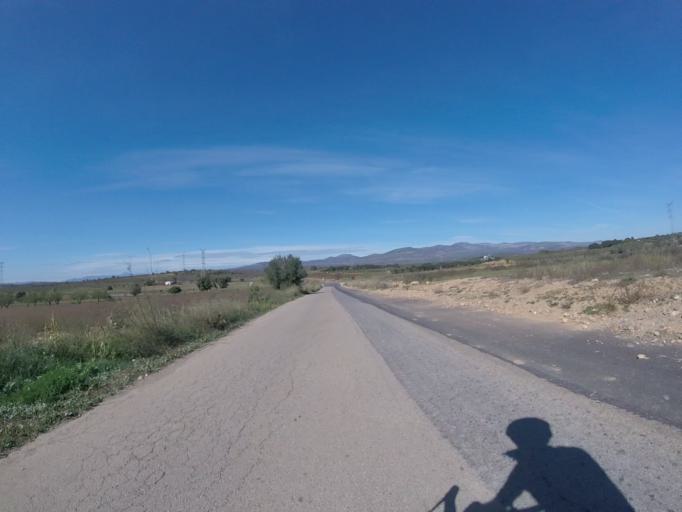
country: ES
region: Valencia
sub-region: Provincia de Castello
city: Benlloch
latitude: 40.2075
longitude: 0.0458
